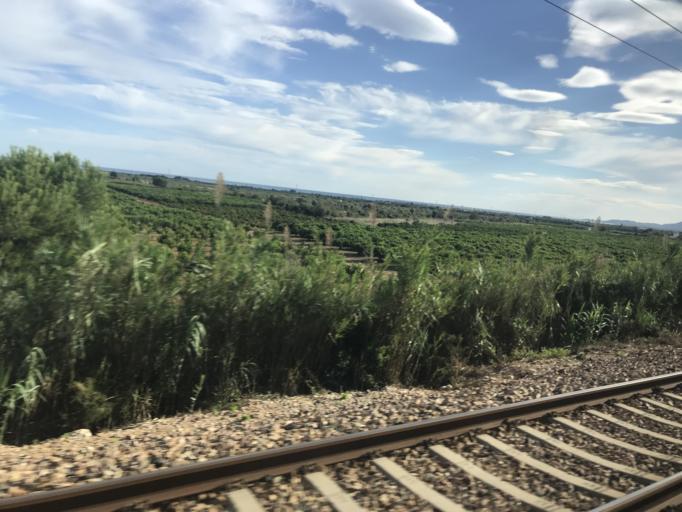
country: ES
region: Valencia
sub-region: Provincia de Castello
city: Torreblanca
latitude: 40.2468
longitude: 0.2357
